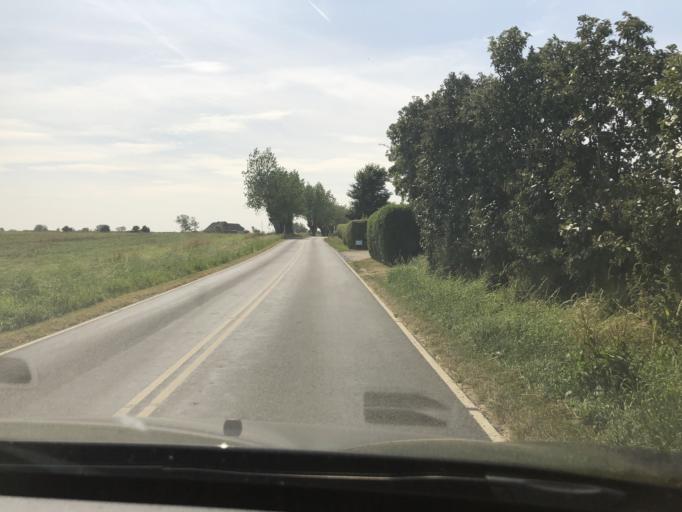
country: DK
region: South Denmark
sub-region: AEro Kommune
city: AEroskobing
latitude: 54.8695
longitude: 10.3899
